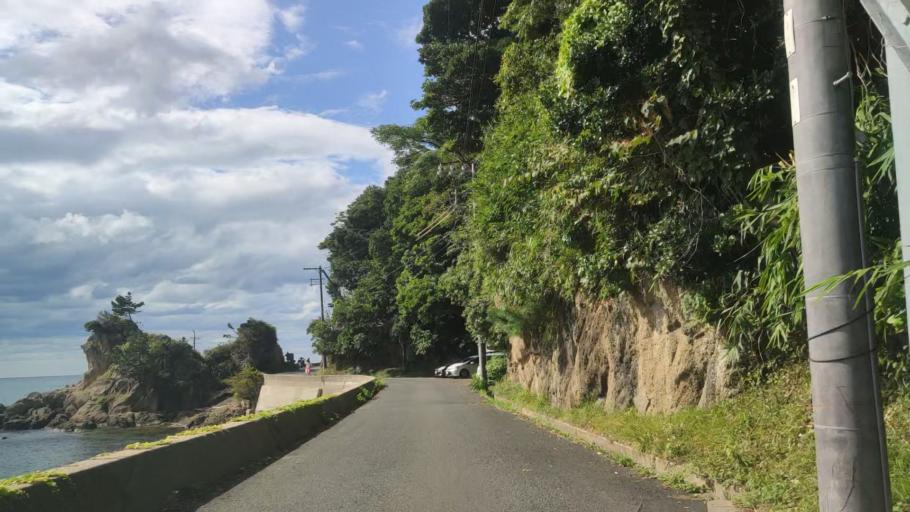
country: JP
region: Hyogo
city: Toyooka
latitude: 35.6705
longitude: 134.9658
